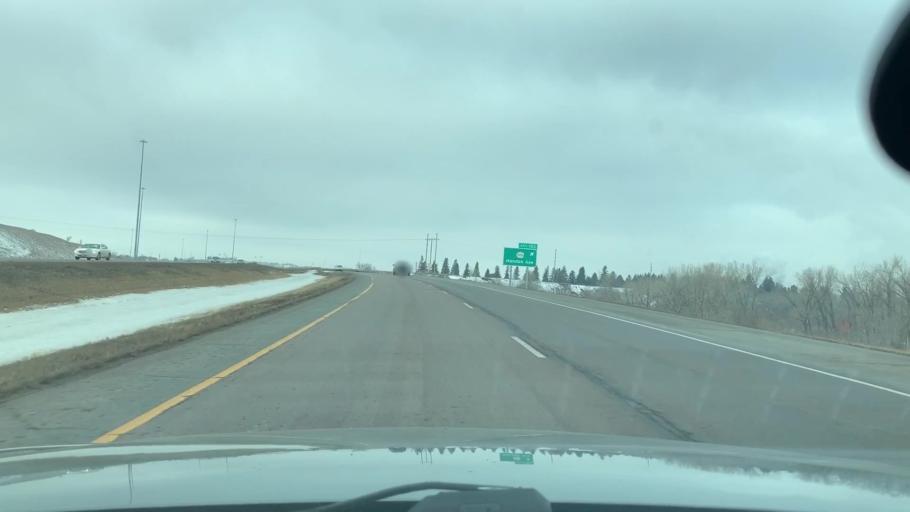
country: US
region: North Dakota
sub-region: Morton County
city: Mandan
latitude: 46.8361
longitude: -100.8664
